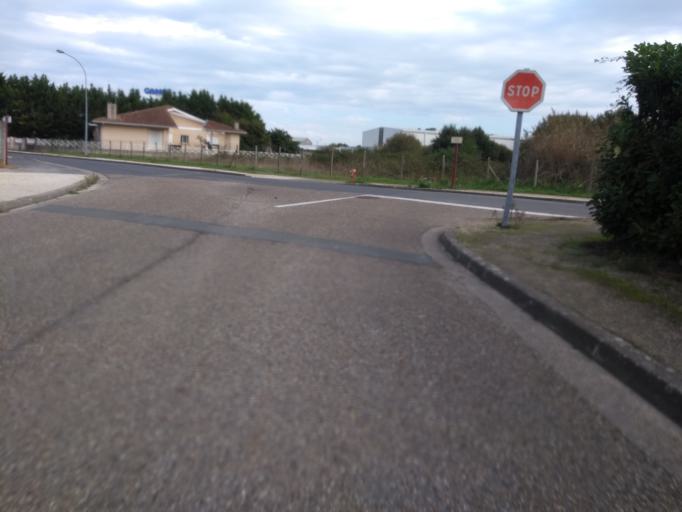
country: FR
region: Aquitaine
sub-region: Departement de la Gironde
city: Canejan
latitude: 44.7715
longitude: -0.6547
